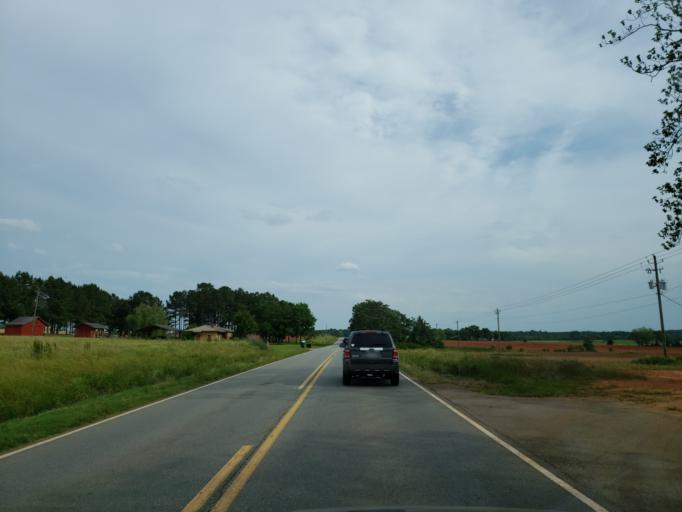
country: US
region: Georgia
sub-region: Dooly County
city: Vienna
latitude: 32.1284
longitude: -83.8682
